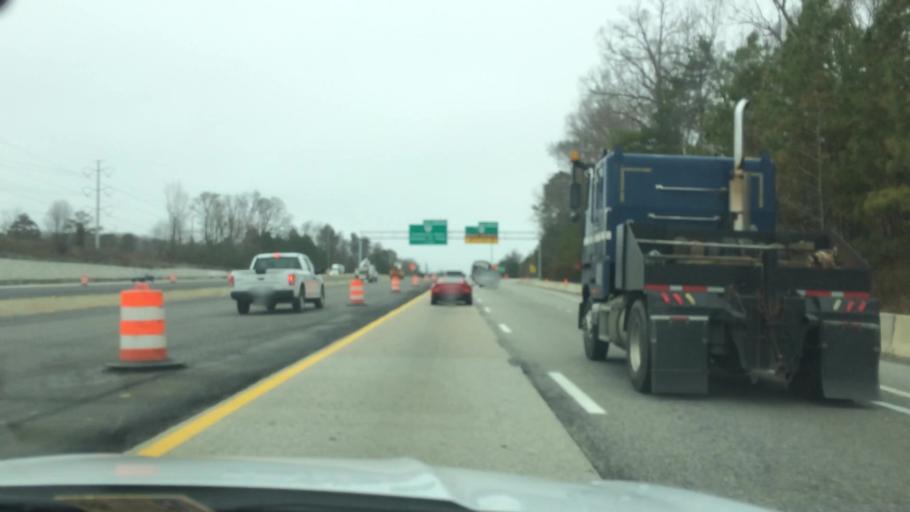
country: US
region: Virginia
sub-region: City of Williamsburg
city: Williamsburg
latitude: 37.2447
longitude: -76.6363
